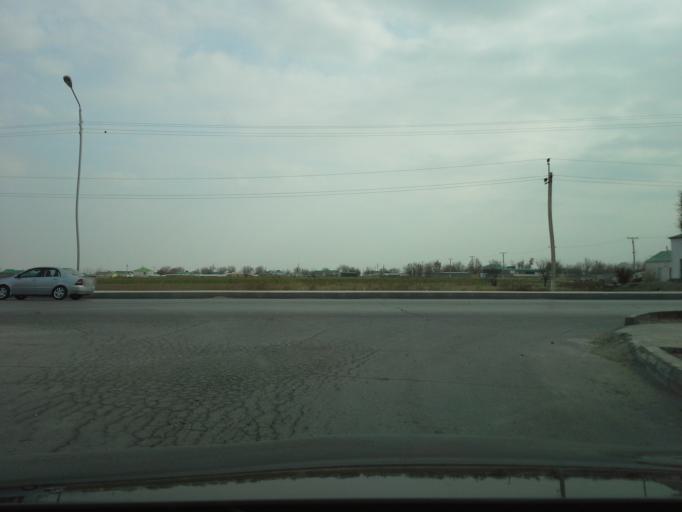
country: TM
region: Ahal
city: Abadan
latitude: 38.0355
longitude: 58.2706
